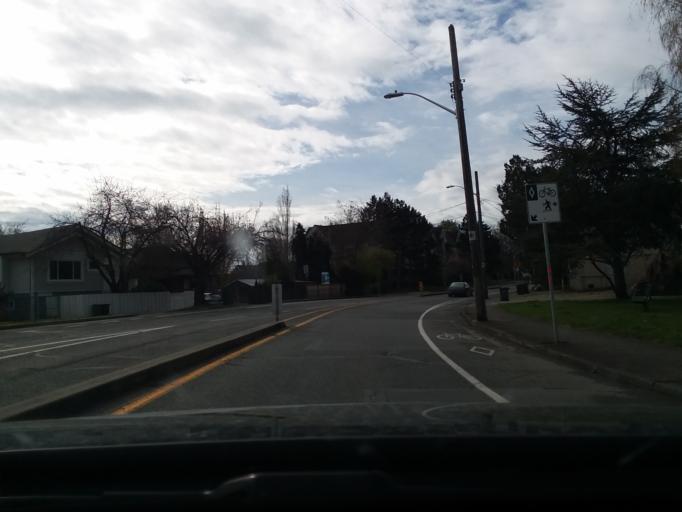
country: CA
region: British Columbia
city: Oak Bay
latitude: 48.4324
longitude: -123.3332
